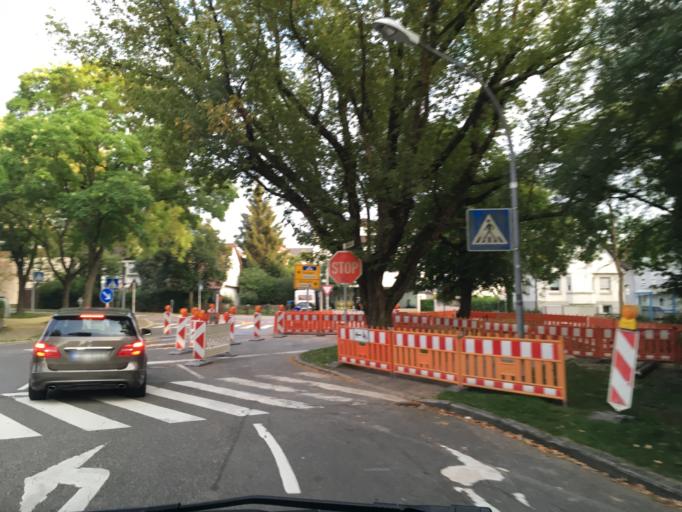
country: DE
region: Baden-Wuerttemberg
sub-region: Regierungsbezirk Stuttgart
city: Sindelfingen
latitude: 48.7092
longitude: 9.0103
